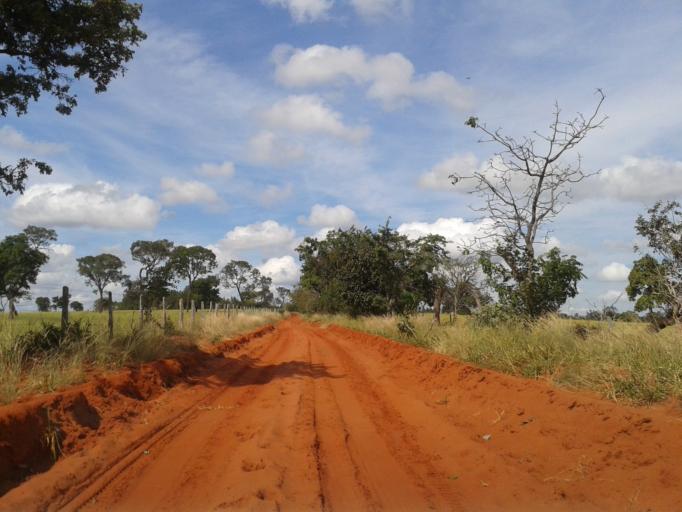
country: BR
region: Minas Gerais
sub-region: Campina Verde
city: Campina Verde
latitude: -19.4494
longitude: -49.6460
